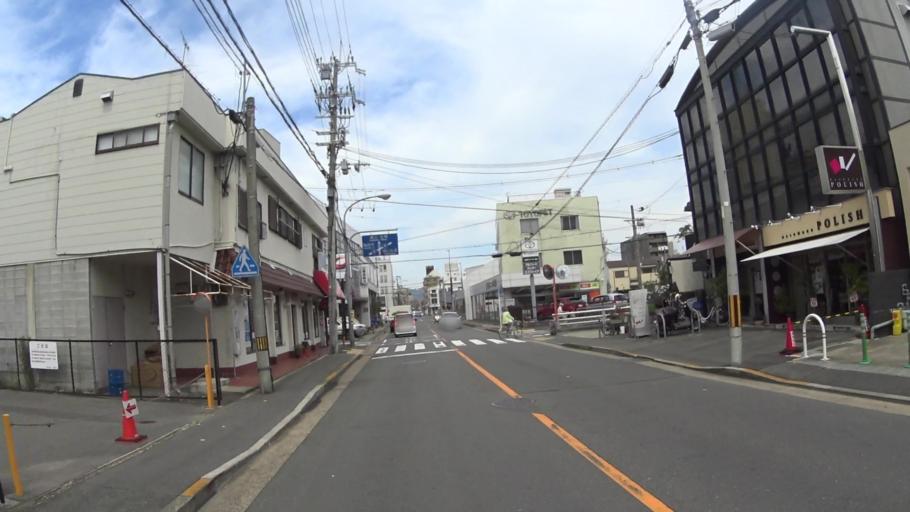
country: JP
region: Kyoto
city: Muko
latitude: 34.9813
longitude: 135.6934
